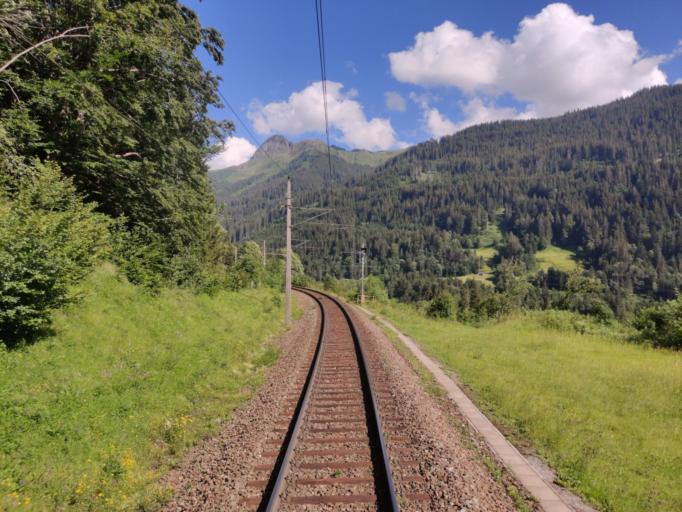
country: AT
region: Vorarlberg
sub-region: Politischer Bezirk Bludenz
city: Klosterle
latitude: 47.1322
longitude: 10.0398
